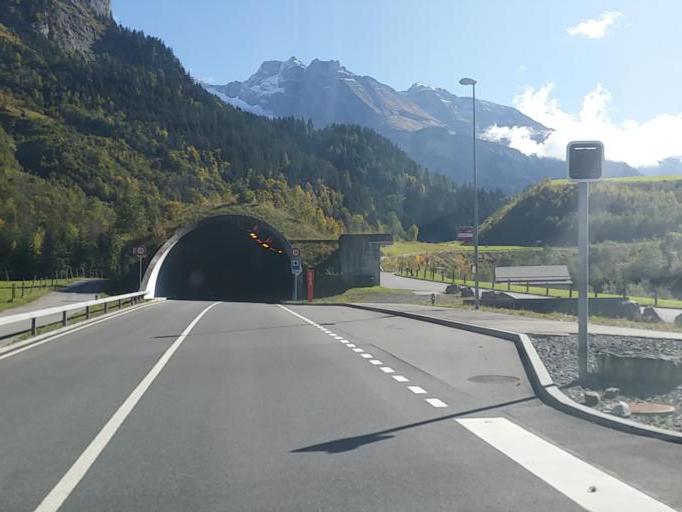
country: CH
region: Bern
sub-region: Frutigen-Niedersimmental District
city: Kandersteg
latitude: 46.5229
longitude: 7.6772
